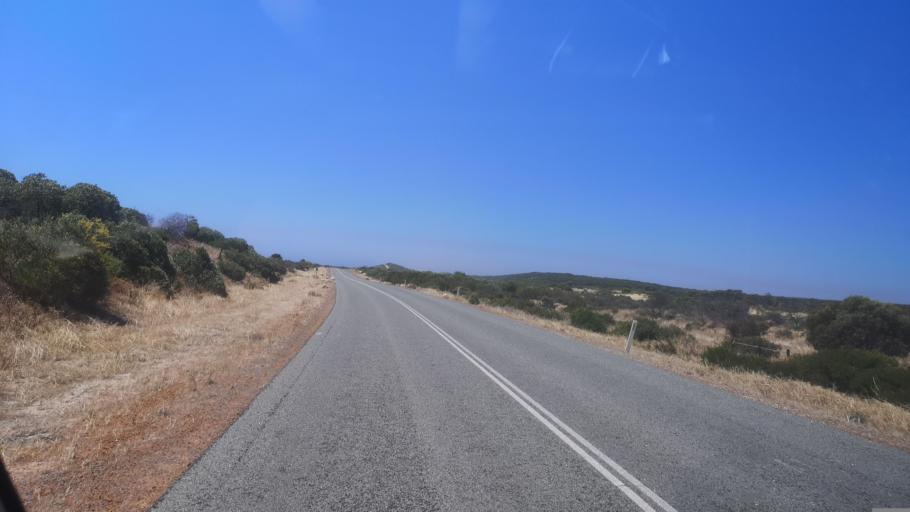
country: AU
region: Western Australia
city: Port Denison
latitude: -29.6734
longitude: 114.9609
